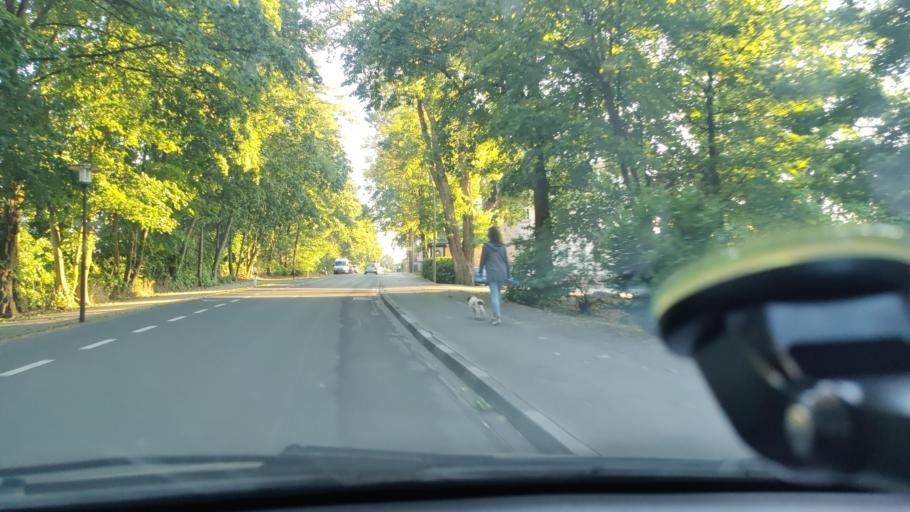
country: DE
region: North Rhine-Westphalia
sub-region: Regierungsbezirk Munster
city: Klein Reken
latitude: 51.8004
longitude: 7.0479
